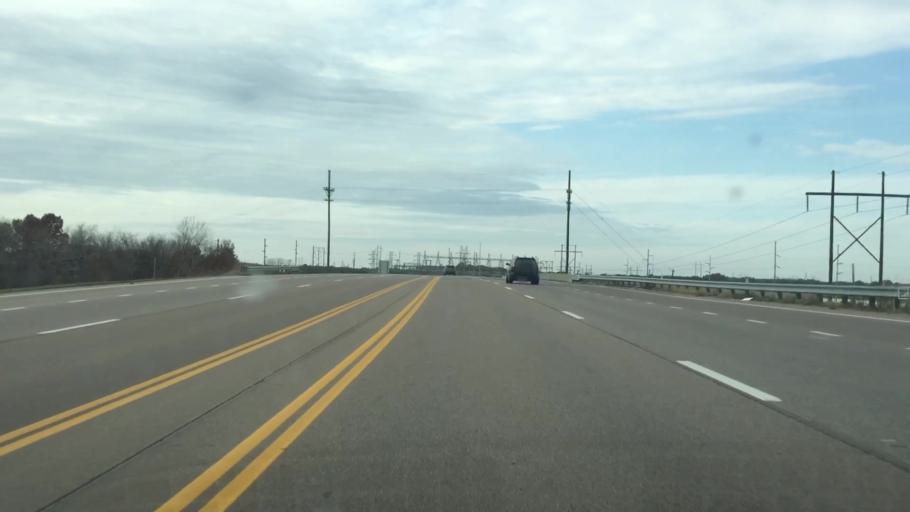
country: US
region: Missouri
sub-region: Henry County
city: Clinton
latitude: 38.3855
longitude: -93.7543
